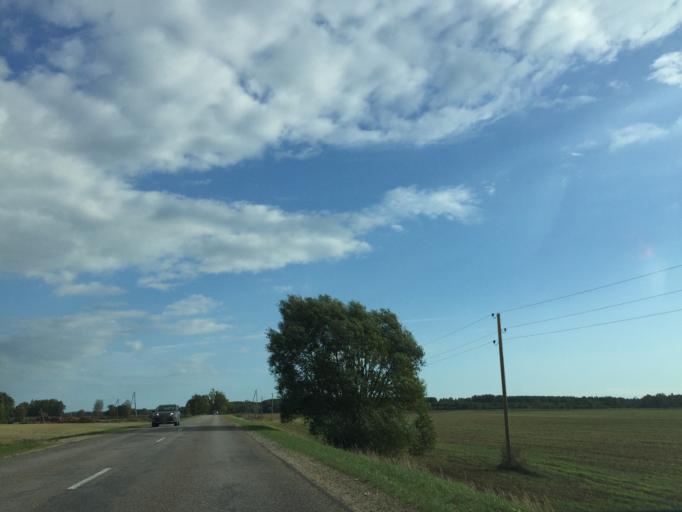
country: LV
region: Limbazu Rajons
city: Limbazi
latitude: 57.5076
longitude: 24.5052
